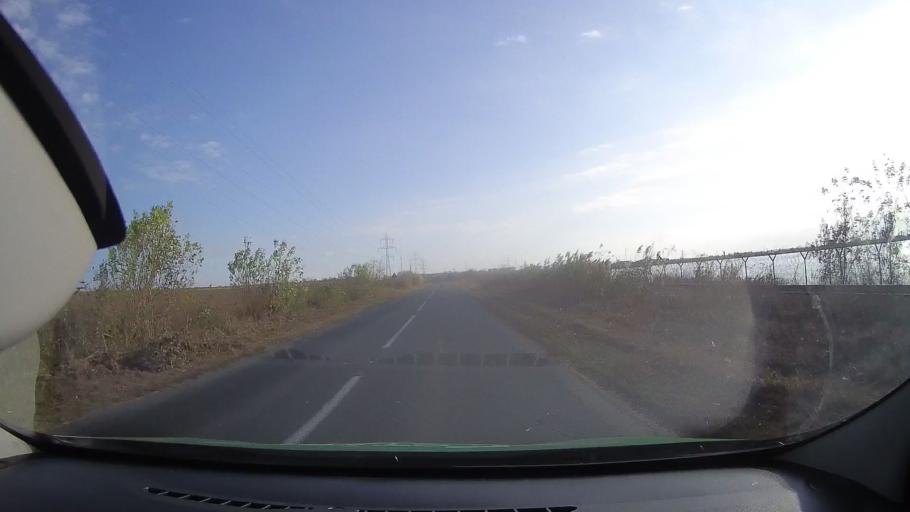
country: RO
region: Constanta
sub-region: Comuna Corbu
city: Corbu
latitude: 44.3651
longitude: 28.6727
